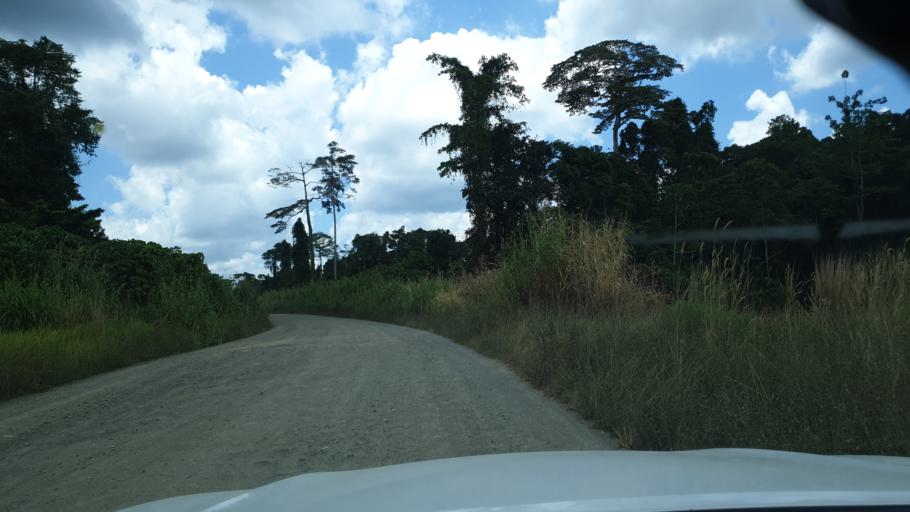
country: PG
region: East Sepik
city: Angoram
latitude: -3.8170
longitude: 143.8517
